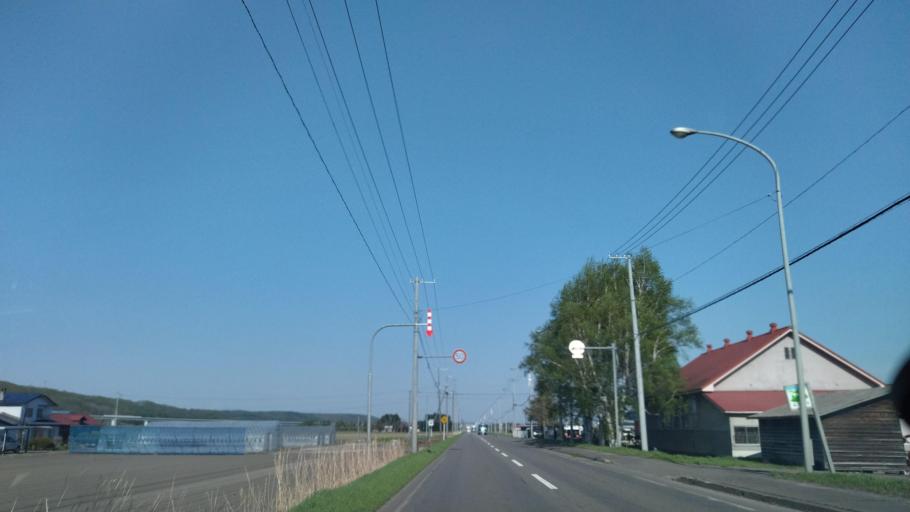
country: JP
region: Hokkaido
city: Obihiro
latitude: 42.9440
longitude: 143.0913
